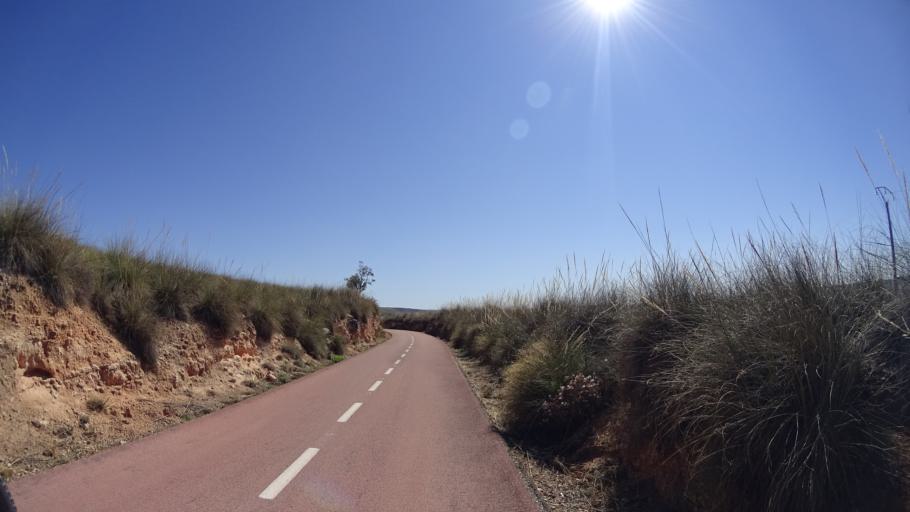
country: ES
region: Madrid
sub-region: Provincia de Madrid
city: Morata de Tajuna
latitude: 40.2254
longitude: -3.4699
